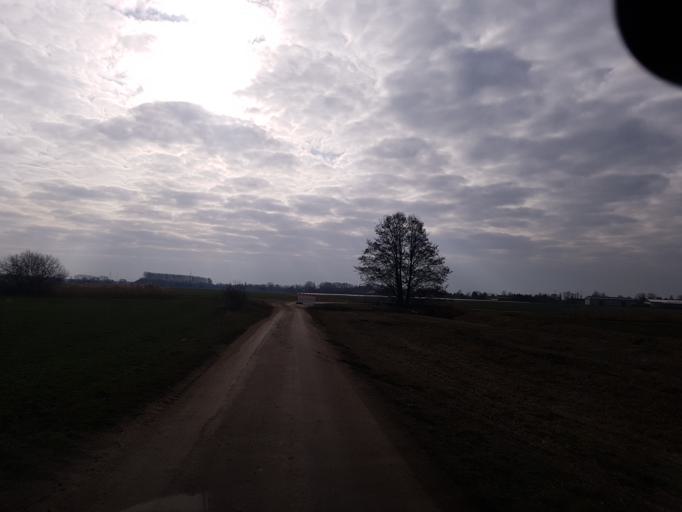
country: DE
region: Brandenburg
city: Doberlug-Kirchhain
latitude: 51.6600
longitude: 13.5443
